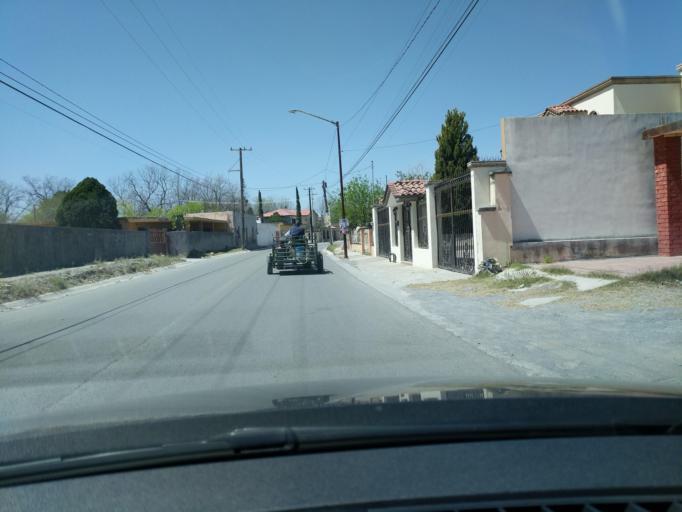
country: MX
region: Nuevo Leon
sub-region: Apodaca
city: Artemio Trevino
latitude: 25.8123
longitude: -100.1443
